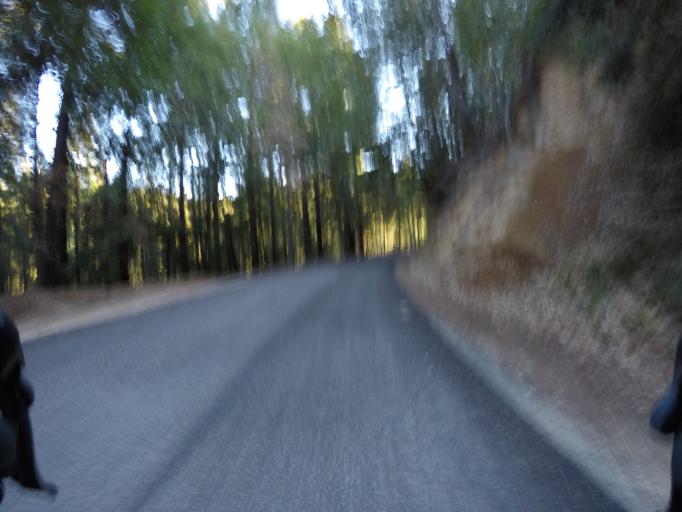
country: US
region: California
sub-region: Santa Cruz County
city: Lompico
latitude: 37.1364
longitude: -122.0225
